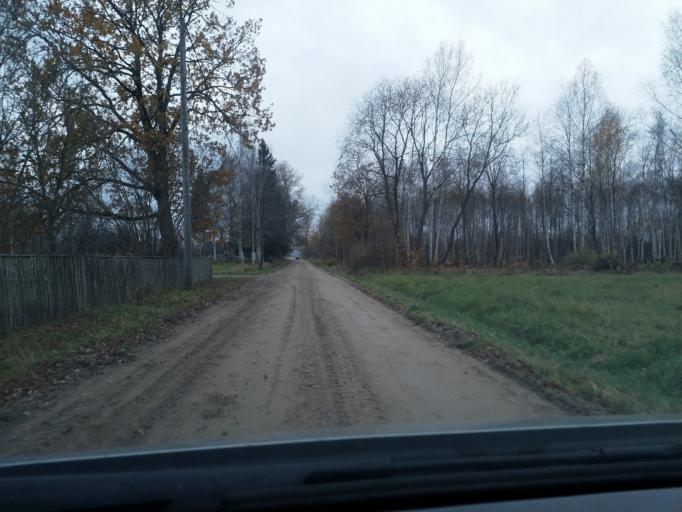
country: LV
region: Kuldigas Rajons
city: Kuldiga
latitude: 56.9610
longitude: 21.9947
